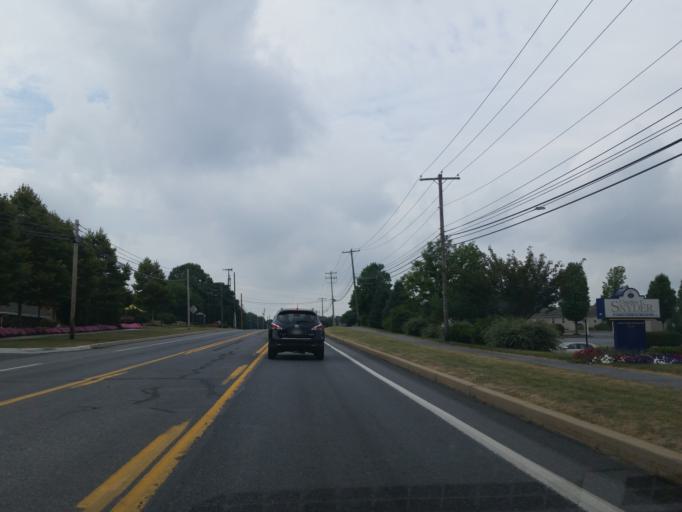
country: US
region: Pennsylvania
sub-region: Lancaster County
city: Lititz
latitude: 40.1121
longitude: -76.3056
